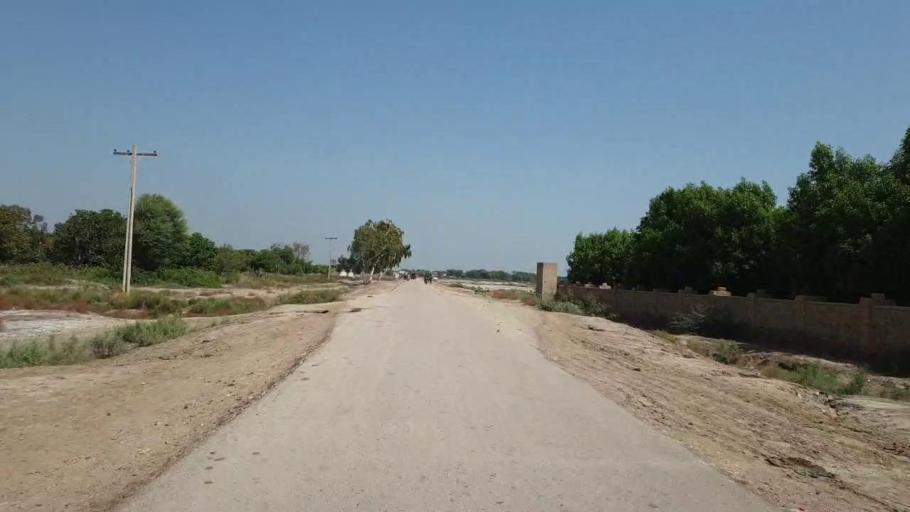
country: PK
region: Sindh
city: Hyderabad
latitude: 25.4450
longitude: 68.4108
